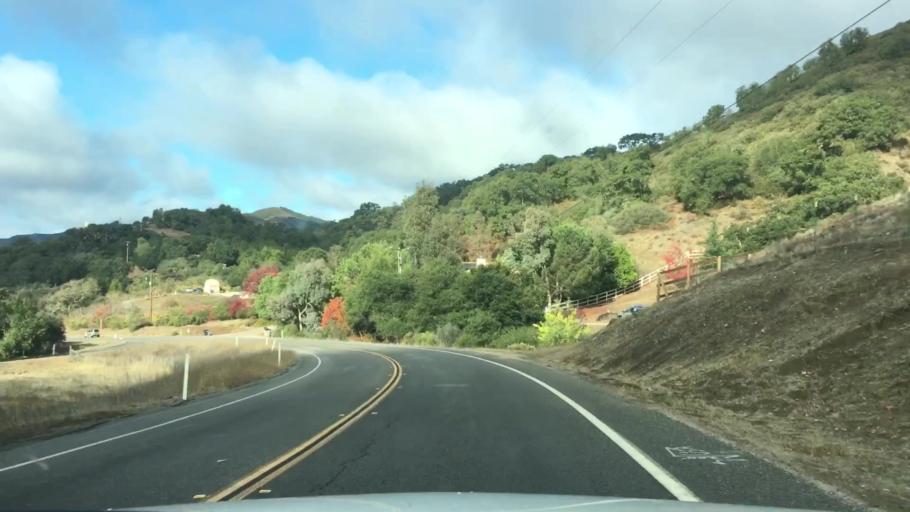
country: US
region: California
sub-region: San Luis Obispo County
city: Atascadero
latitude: 35.4591
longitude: -120.7192
